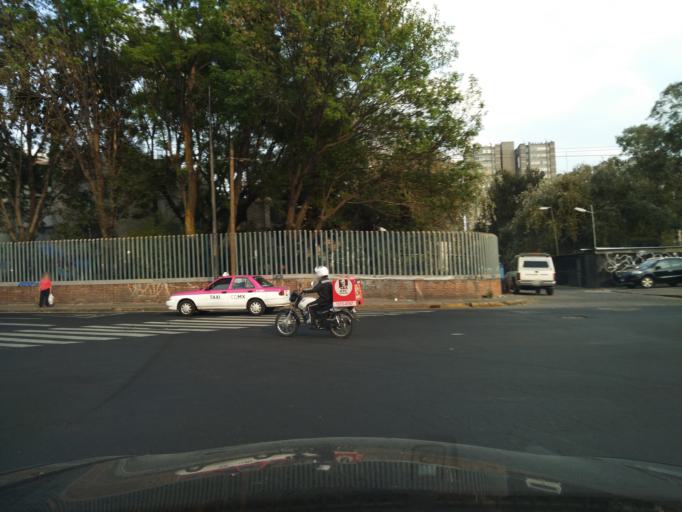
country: MX
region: Mexico City
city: Tlalpan
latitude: 19.3154
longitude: -99.1246
